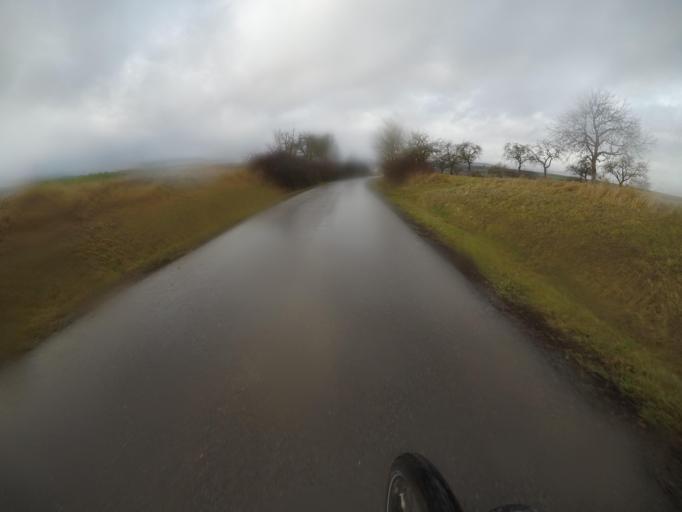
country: DE
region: Baden-Wuerttemberg
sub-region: Regierungsbezirk Stuttgart
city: Eberdingen
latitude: 48.9063
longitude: 8.9943
